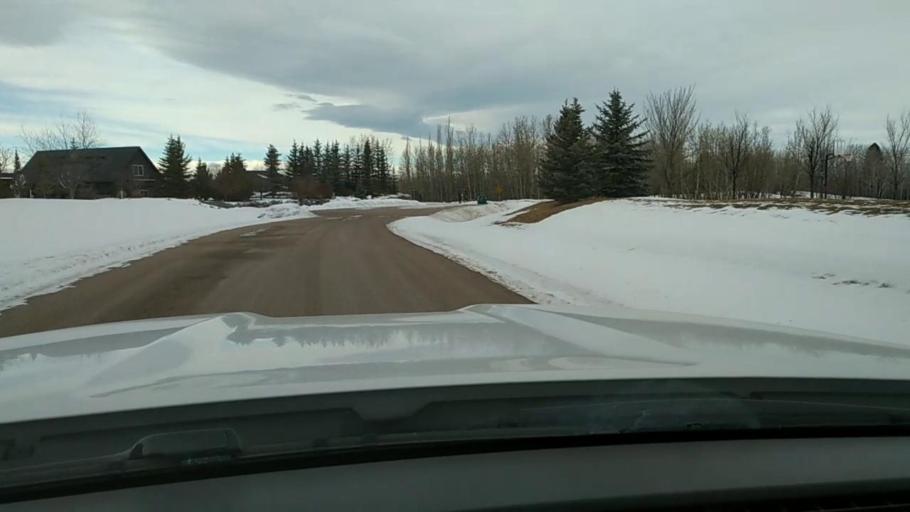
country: CA
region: Alberta
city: Cochrane
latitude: 51.1855
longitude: -114.2615
